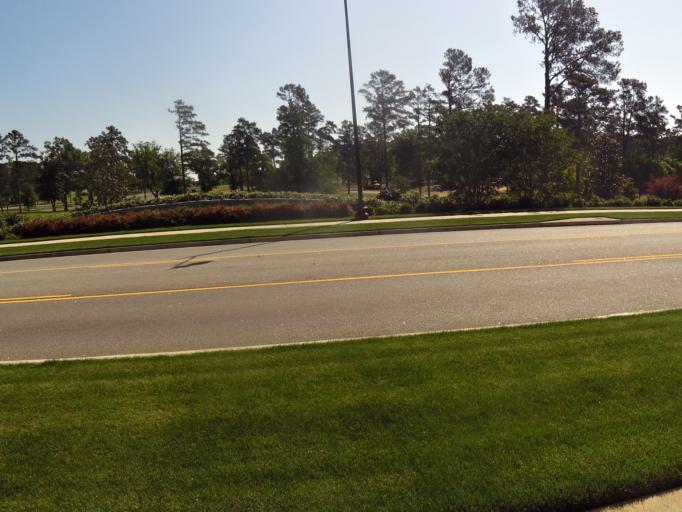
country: US
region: Georgia
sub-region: Columbia County
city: Martinez
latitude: 33.5034
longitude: -82.0316
